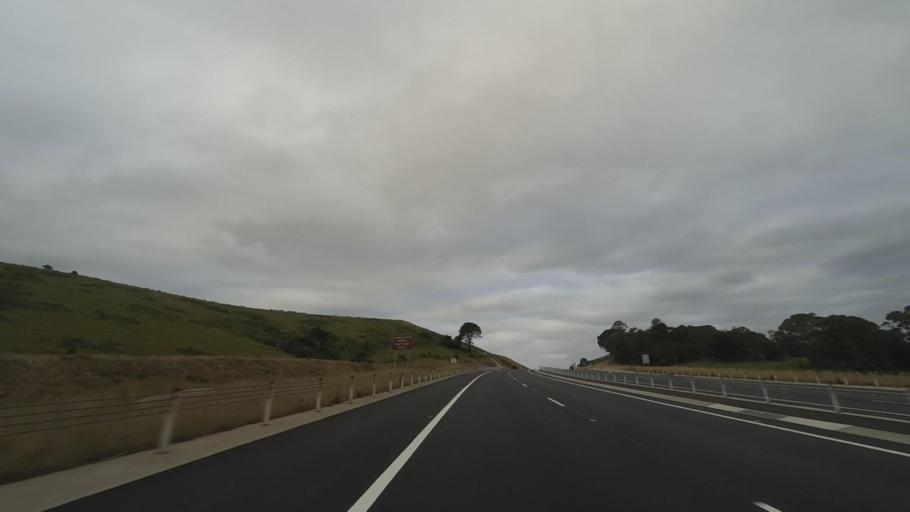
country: AU
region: New South Wales
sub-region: Kiama
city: Gerringong
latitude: -34.7484
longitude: 150.7990
